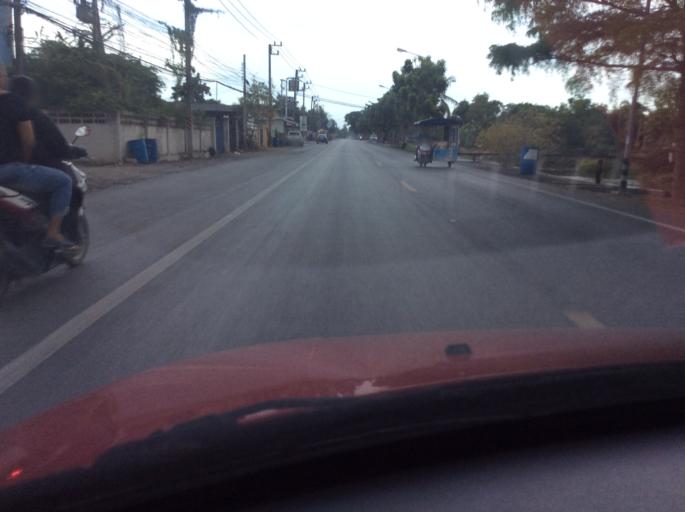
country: TH
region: Pathum Thani
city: Lam Luk Ka
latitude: 13.9499
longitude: 100.7270
